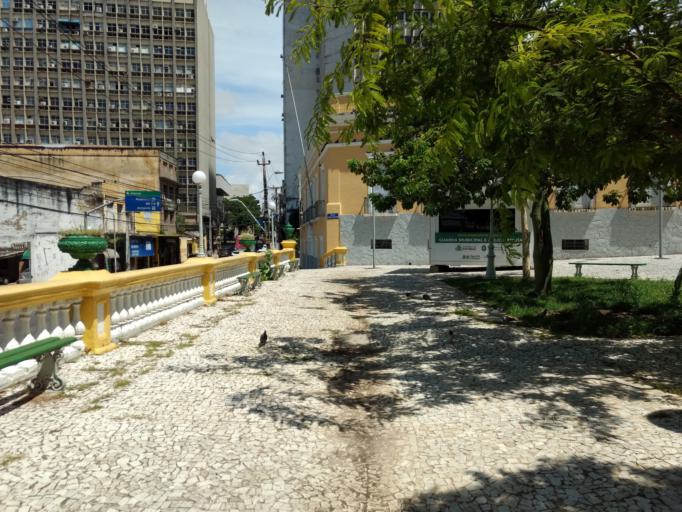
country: BR
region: Ceara
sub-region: Fortaleza
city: Fortaleza
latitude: -3.7270
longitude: -38.5260
